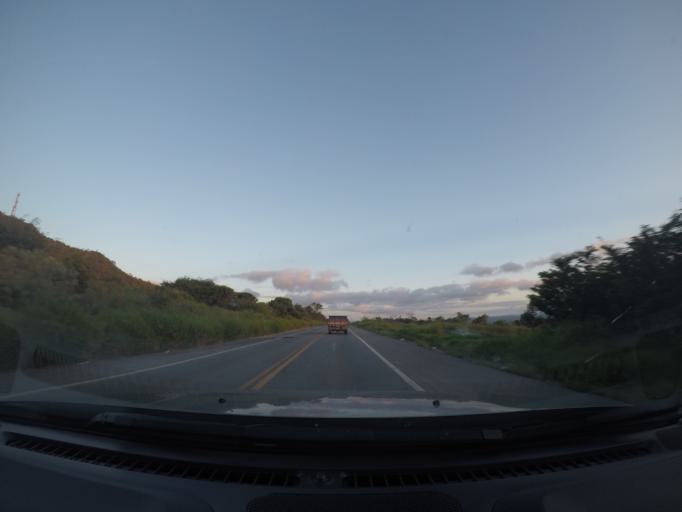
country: BR
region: Bahia
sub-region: Seabra
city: Seabra
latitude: -12.4280
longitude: -41.8298
